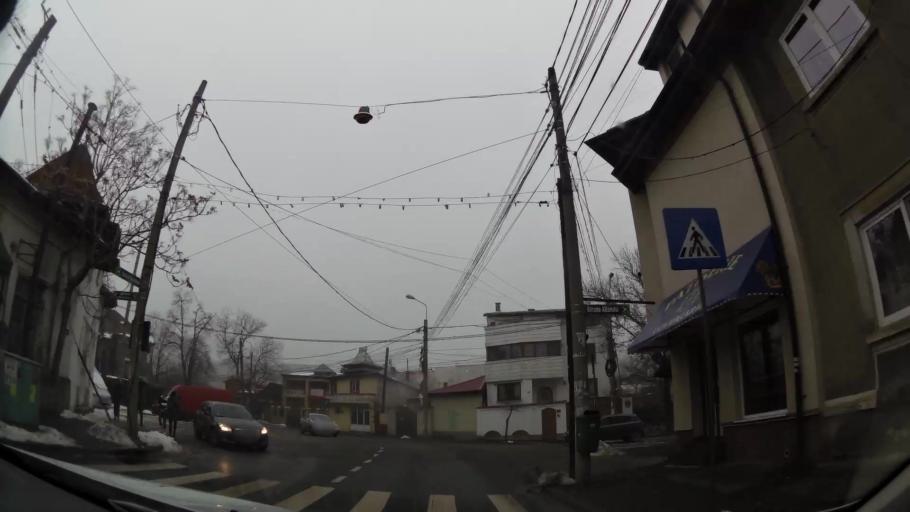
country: RO
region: Ilfov
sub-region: Comuna Chiajna
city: Rosu
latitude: 44.4510
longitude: 26.0547
